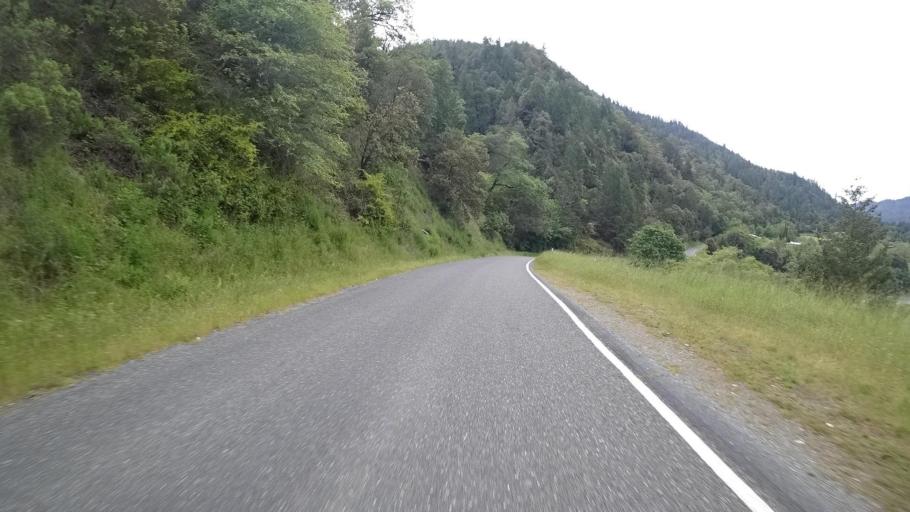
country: US
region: California
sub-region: Humboldt County
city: Willow Creek
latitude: 40.9484
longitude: -123.6113
